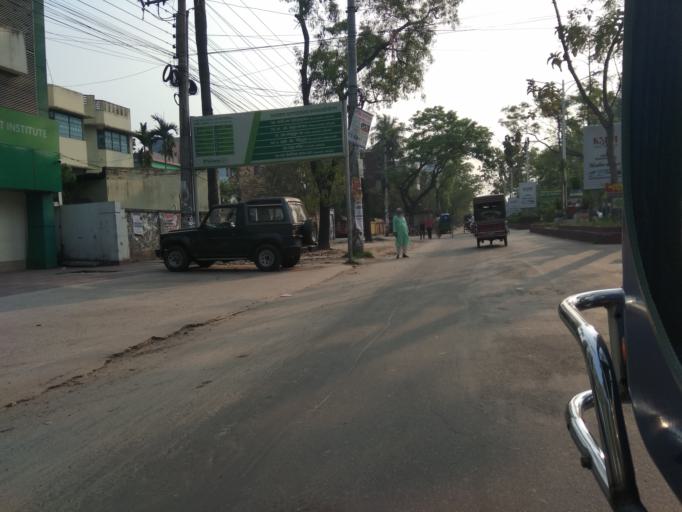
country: BD
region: Khulna
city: Khulna
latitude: 22.8191
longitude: 89.5479
